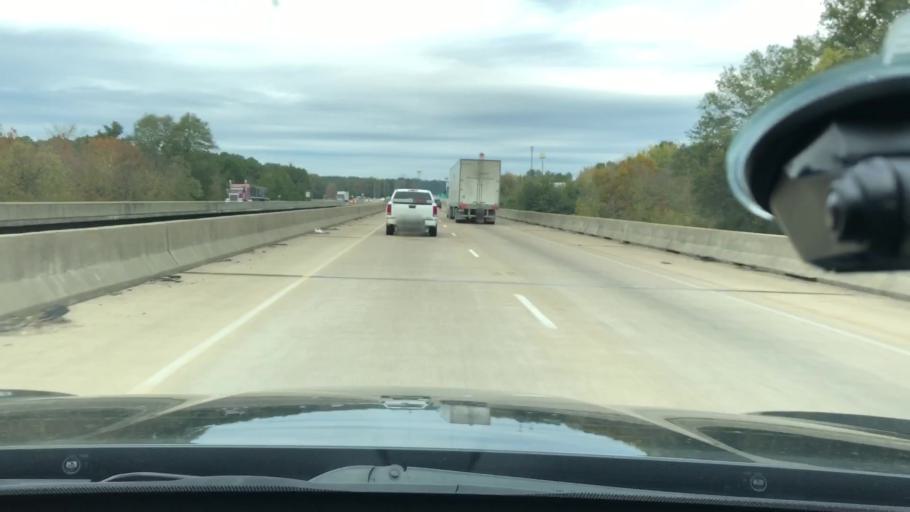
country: US
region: Arkansas
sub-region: Clark County
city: Arkadelphia
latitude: 34.1761
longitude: -93.0740
